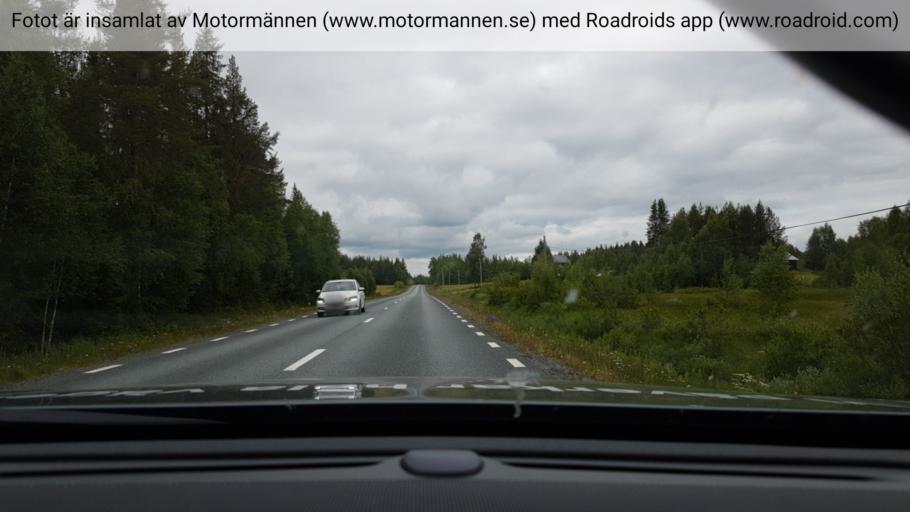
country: SE
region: Vaesterbotten
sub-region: Sorsele Kommun
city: Sorsele
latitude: 65.3864
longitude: 17.5767
